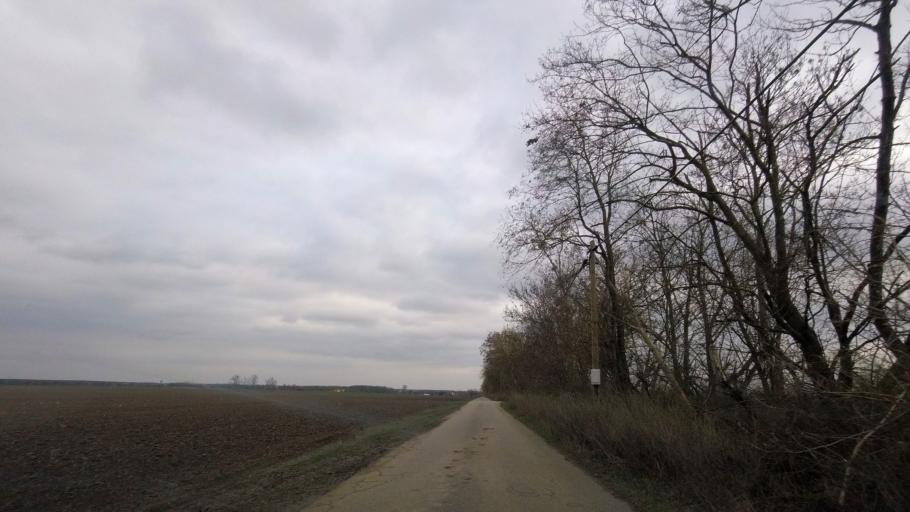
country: DE
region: Saxony-Anhalt
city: Seyda
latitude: 51.9024
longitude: 12.8892
